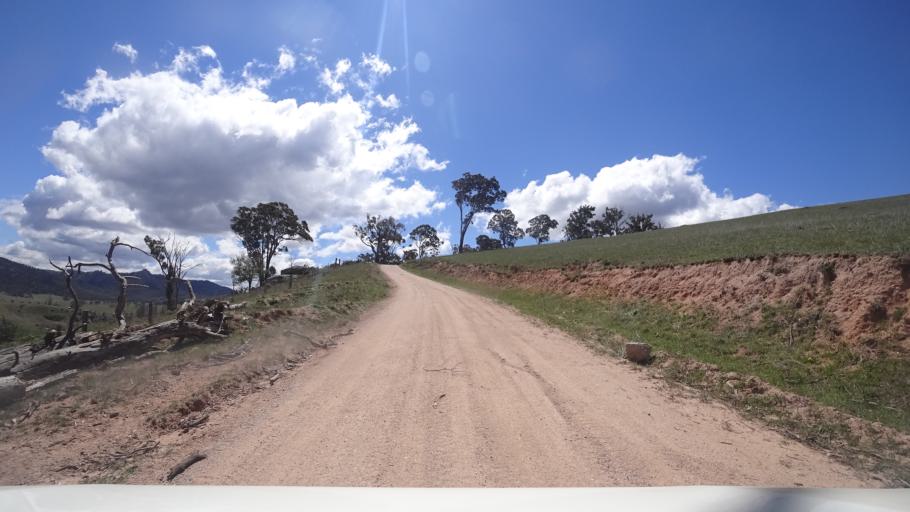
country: AU
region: New South Wales
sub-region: Oberon
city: Oberon
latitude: -33.5729
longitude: 149.9413
